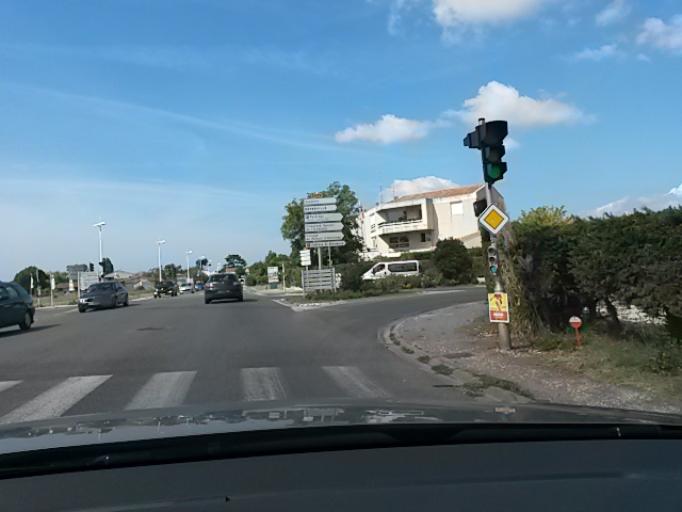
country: FR
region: Poitou-Charentes
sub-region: Departement de la Charente-Maritime
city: Dolus-d'Oleron
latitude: 45.9406
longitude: -1.3134
